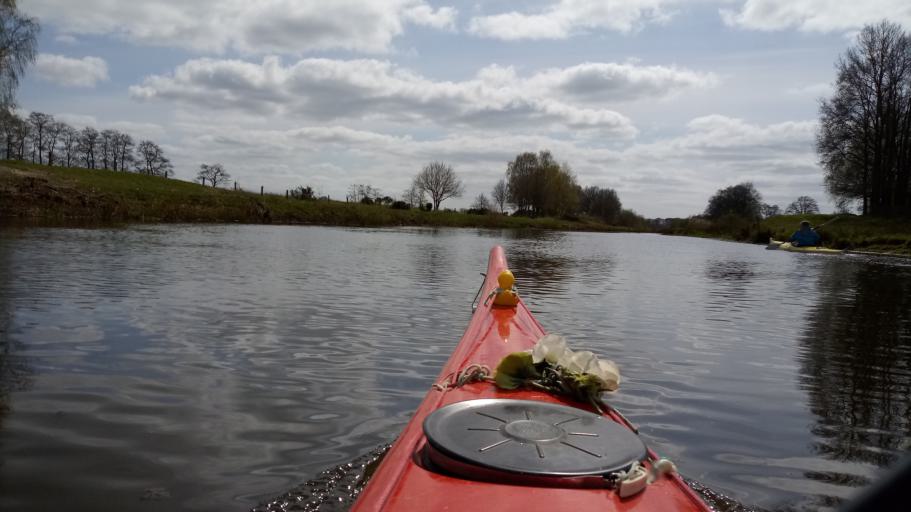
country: NL
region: Overijssel
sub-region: Gemeente Twenterand
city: Den Ham
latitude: 52.4637
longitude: 6.4476
